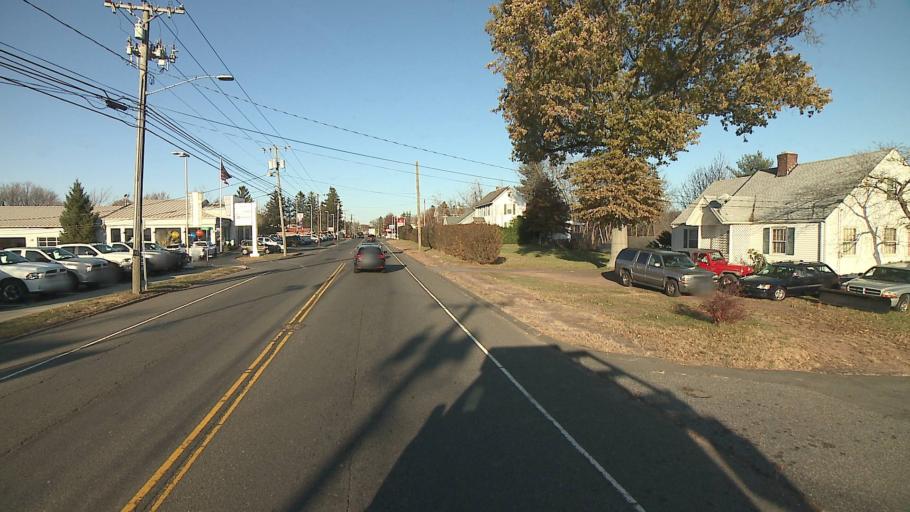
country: US
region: Connecticut
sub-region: New Haven County
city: Meriden
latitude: 41.5181
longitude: -72.8035
